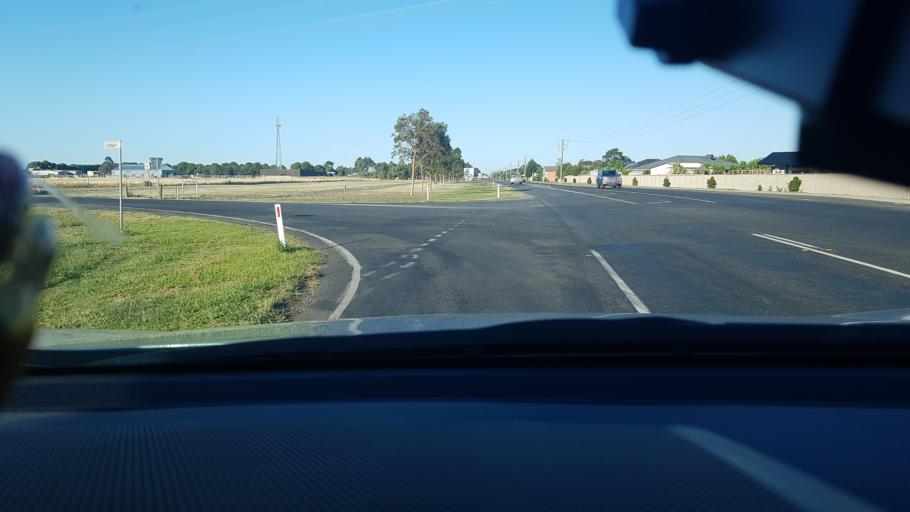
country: AU
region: Victoria
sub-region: Horsham
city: Horsham
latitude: -36.7258
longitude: 142.1686
